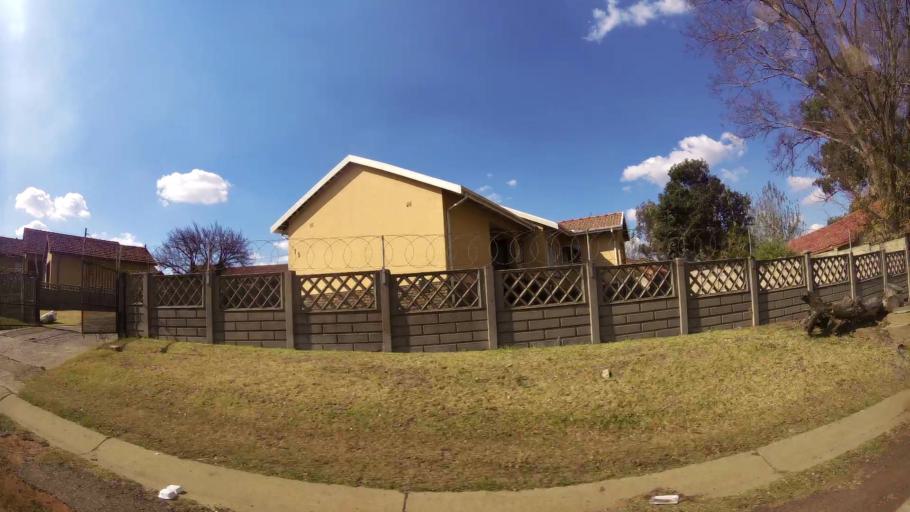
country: ZA
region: Mpumalanga
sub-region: Nkangala District Municipality
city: Witbank
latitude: -25.9287
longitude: 29.2366
